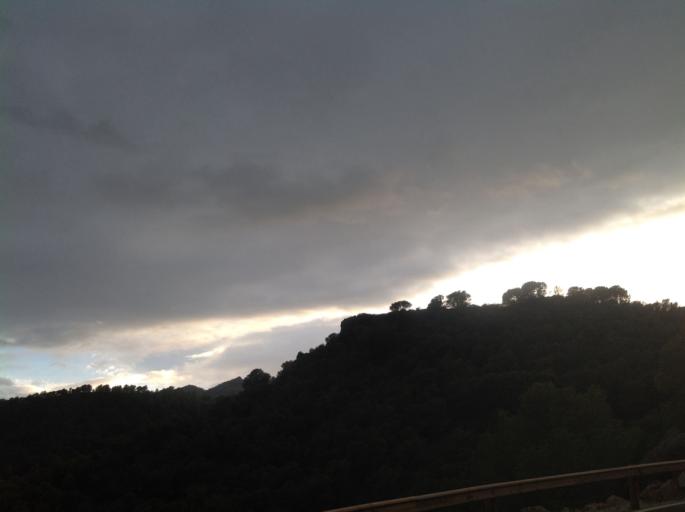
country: ES
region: Andalusia
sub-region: Provincia de Malaga
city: Ardales
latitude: 36.9122
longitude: -4.7919
